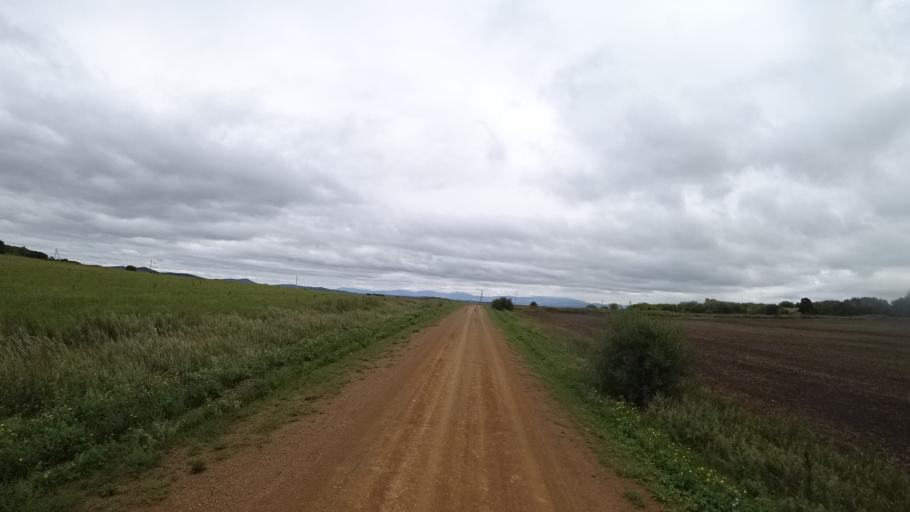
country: RU
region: Primorskiy
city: Chernigovka
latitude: 44.4354
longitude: 132.5899
